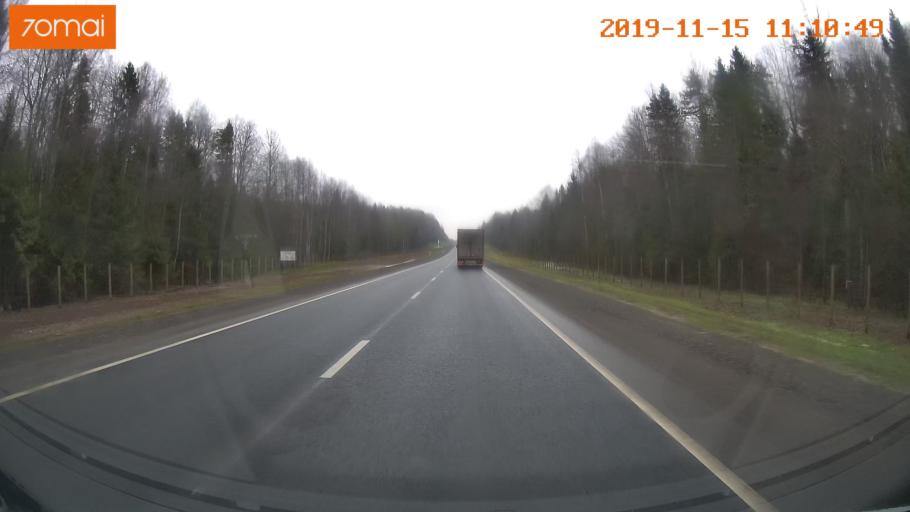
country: RU
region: Vologda
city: Chebsara
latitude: 59.1211
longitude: 39.1297
